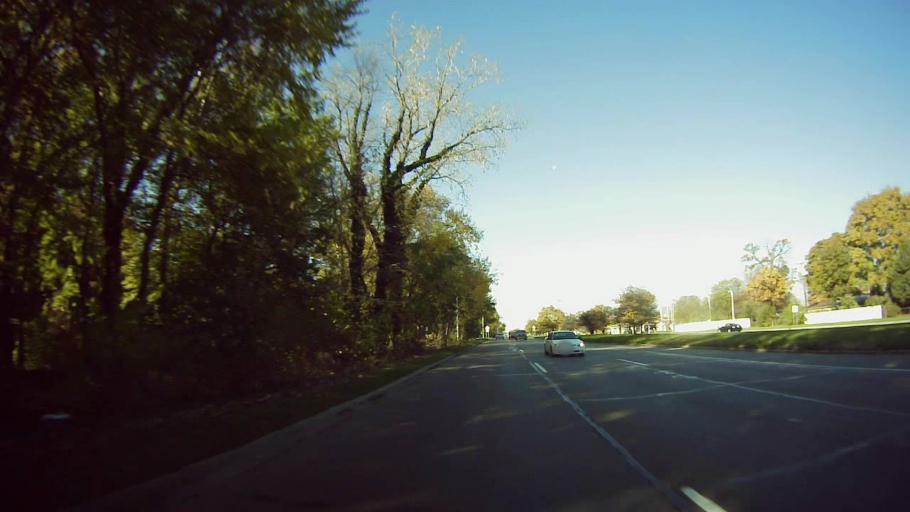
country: US
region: Michigan
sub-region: Wayne County
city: Dearborn Heights
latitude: 42.3270
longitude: -83.2533
